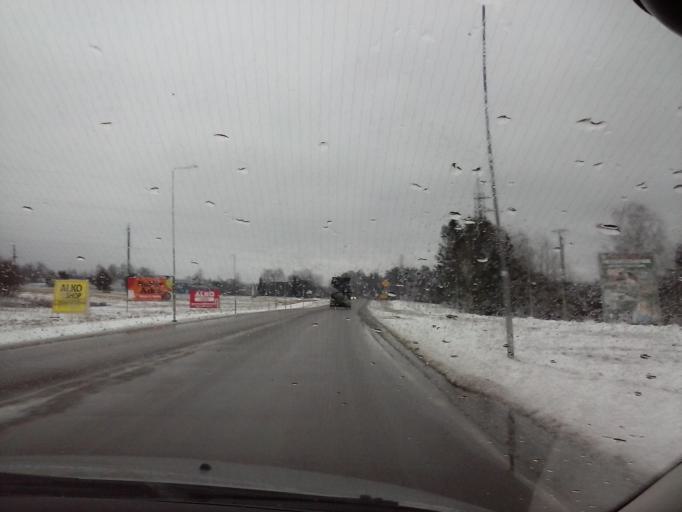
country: EE
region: Valgamaa
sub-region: Valga linn
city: Valga
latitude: 57.7904
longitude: 26.0509
